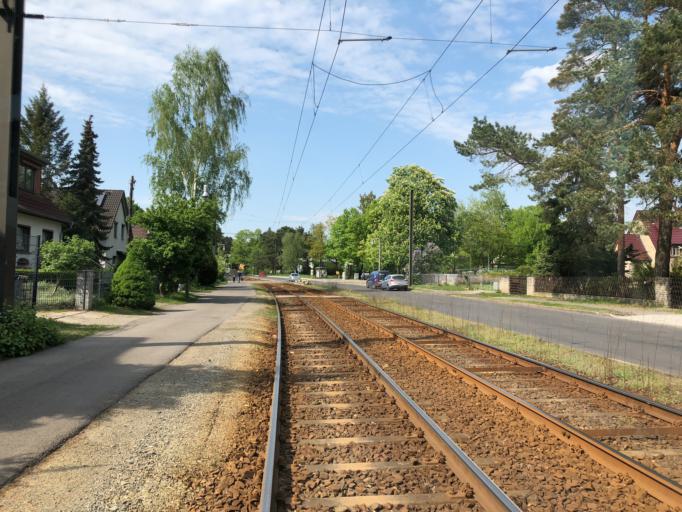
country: DE
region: Berlin
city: Schmockwitz
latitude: 52.3904
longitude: 13.6351
